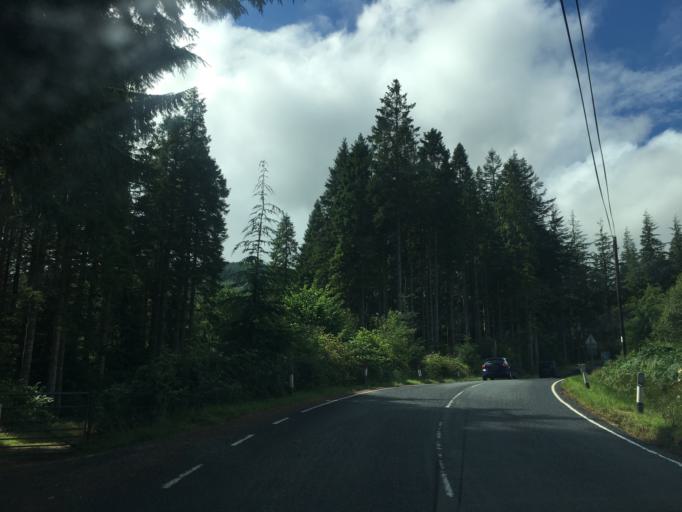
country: GB
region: Scotland
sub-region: Argyll and Bute
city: Dunoon
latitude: 55.9890
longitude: -4.9947
